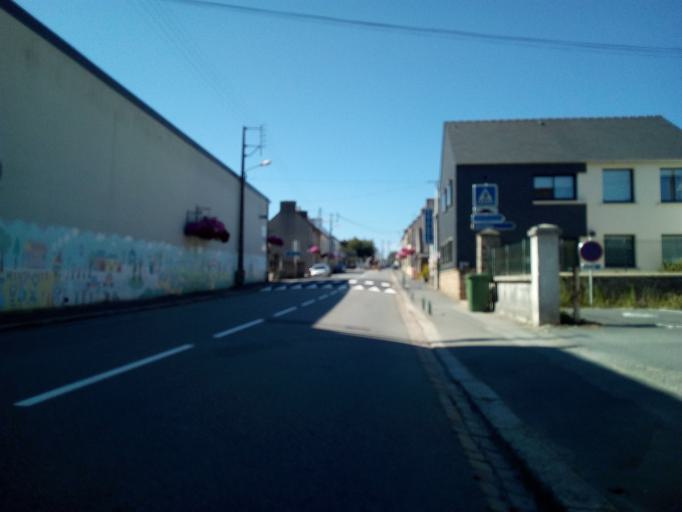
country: FR
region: Brittany
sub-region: Departement du Finistere
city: Landivisiau
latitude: 48.5117
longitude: -4.0704
